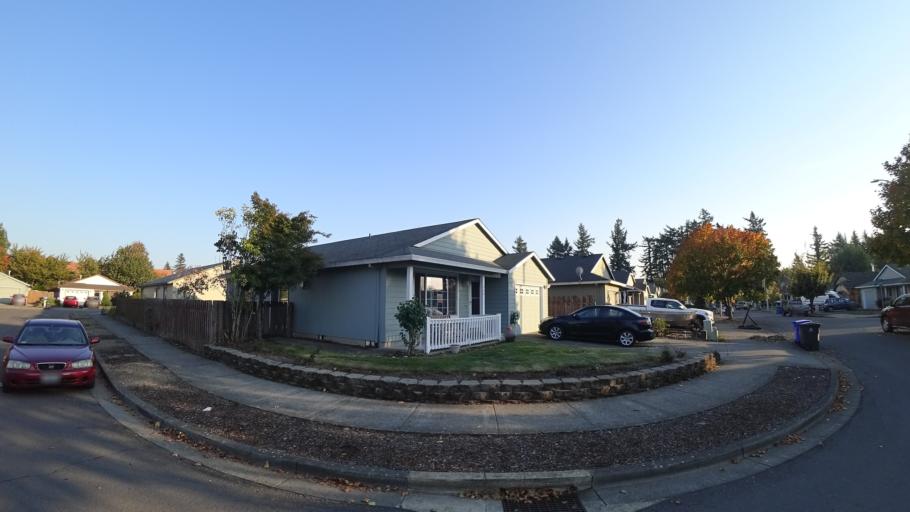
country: US
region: Oregon
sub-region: Multnomah County
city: Gresham
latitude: 45.5139
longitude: -122.4360
